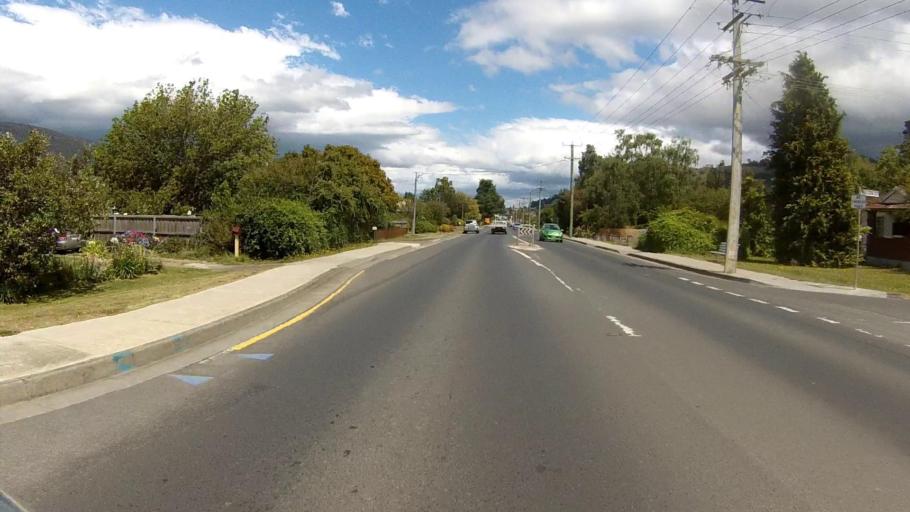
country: AU
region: Tasmania
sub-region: Huon Valley
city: Huonville
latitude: -43.0237
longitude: 147.0523
